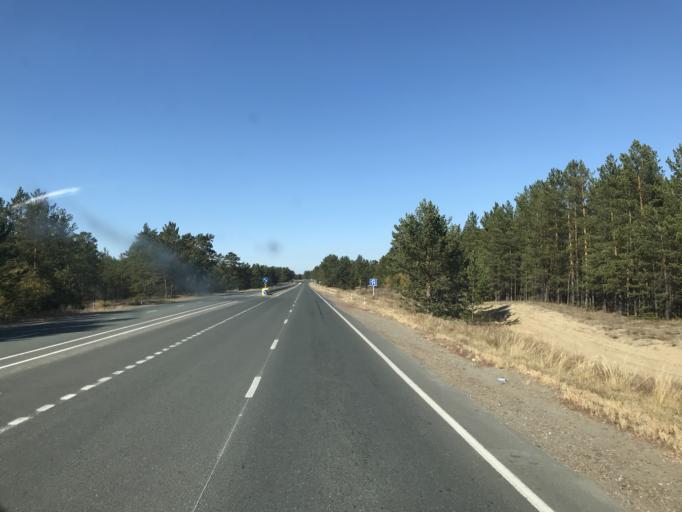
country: KZ
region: East Kazakhstan
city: Semey
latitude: 50.5012
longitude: 80.1161
